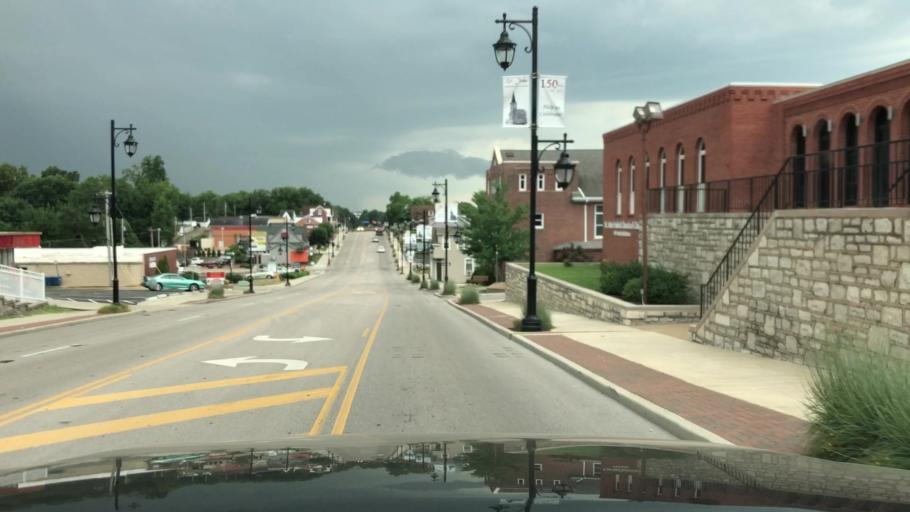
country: US
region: Missouri
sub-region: Saint Charles County
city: Saint Charles
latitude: 38.7801
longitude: -90.4875
